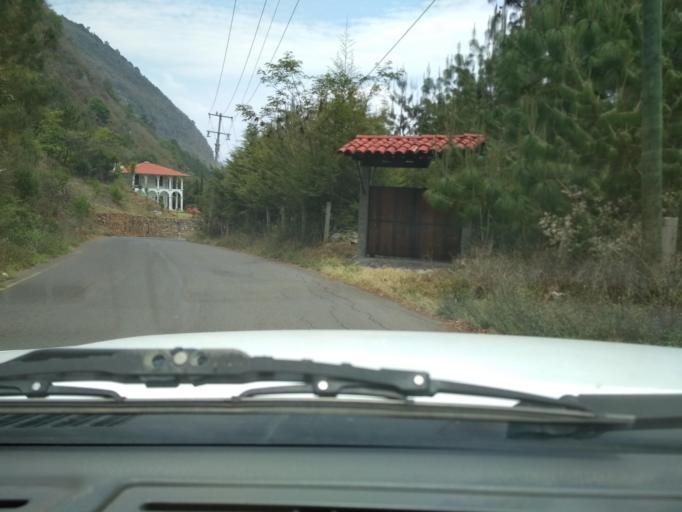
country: MX
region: Veracruz
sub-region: Camerino Z. Mendoza
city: La Cuesta
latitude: 18.7865
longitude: -97.1671
